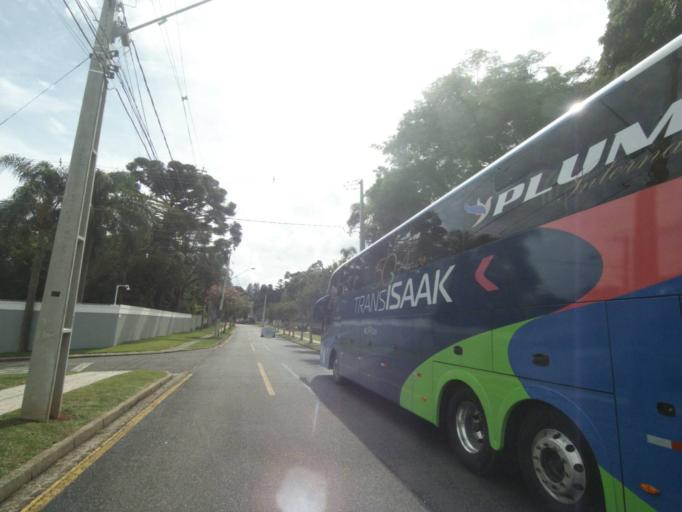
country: BR
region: Parana
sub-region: Curitiba
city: Curitiba
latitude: -25.4449
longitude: -49.3003
